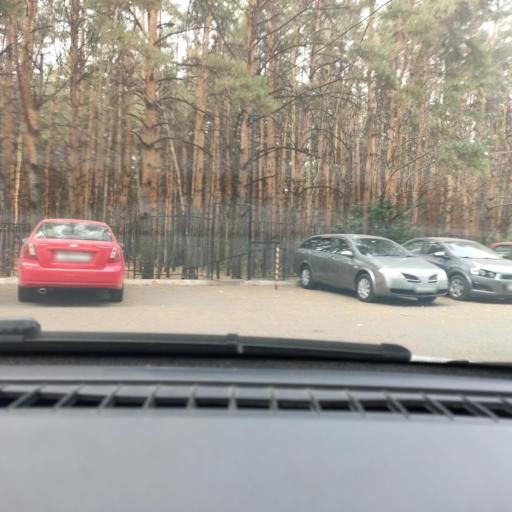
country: RU
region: Voronezj
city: Podgornoye
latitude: 51.7138
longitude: 39.1517
